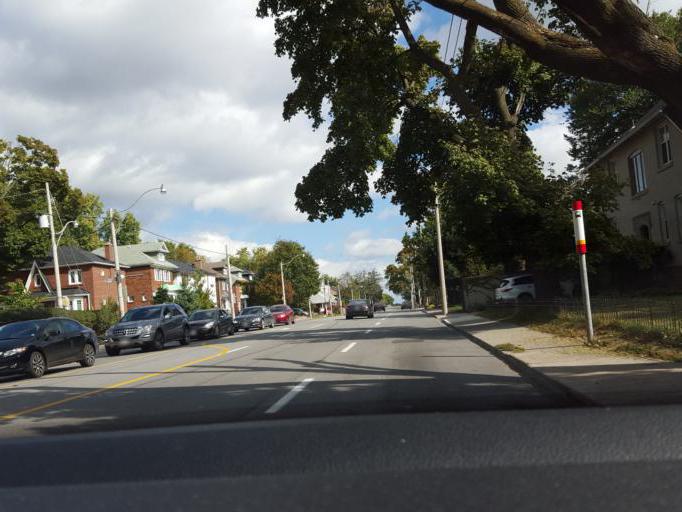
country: CA
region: Ontario
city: Toronto
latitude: 43.7264
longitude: -79.3958
